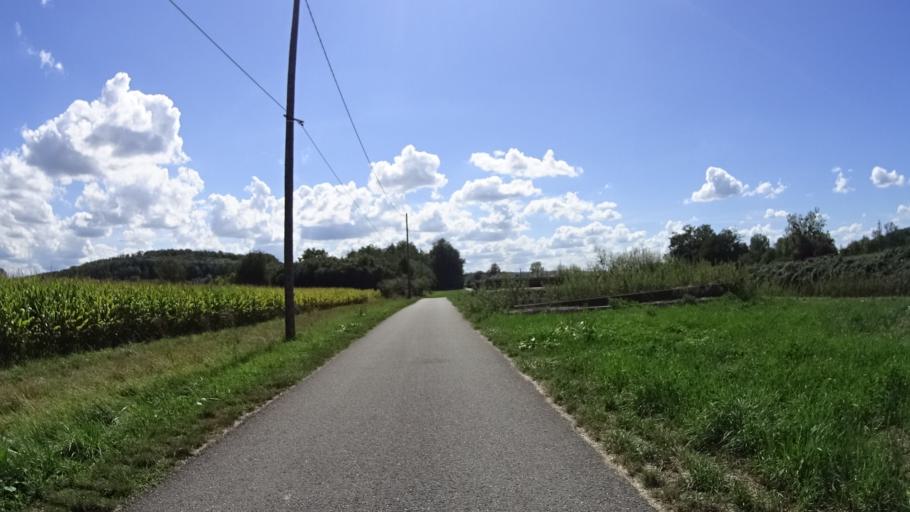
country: FR
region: Alsace
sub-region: Departement du Haut-Rhin
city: Illfurth
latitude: 47.6725
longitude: 7.2582
